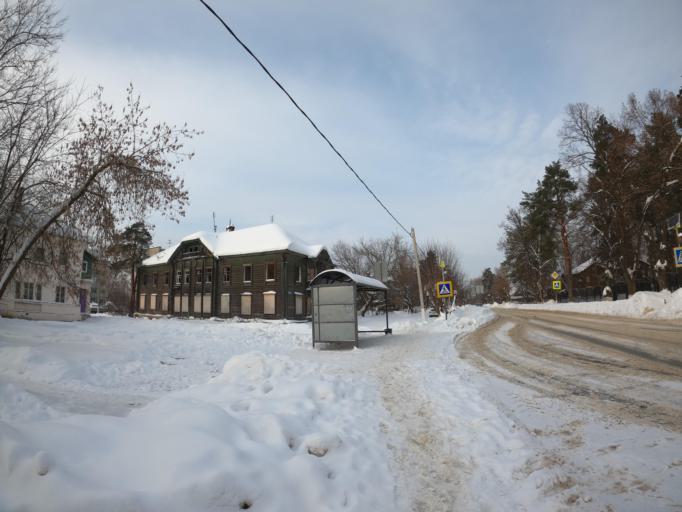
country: RU
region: Moskovskaya
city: Elektrogorsk
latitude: 55.8906
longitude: 38.7721
